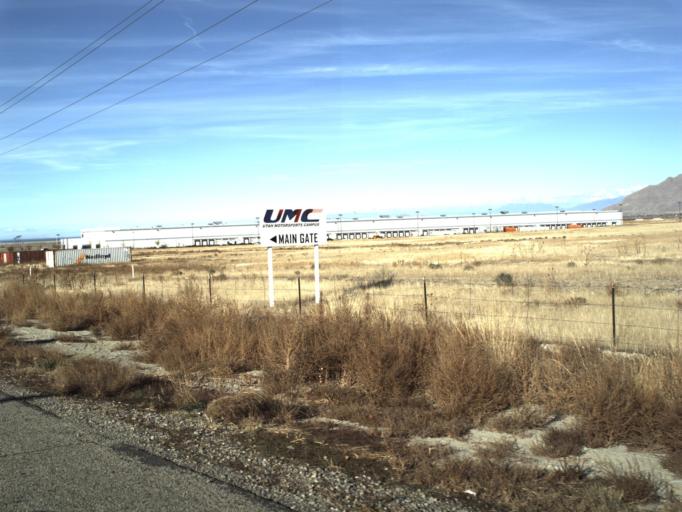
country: US
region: Utah
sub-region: Tooele County
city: Erda
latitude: 40.5819
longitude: -112.3696
